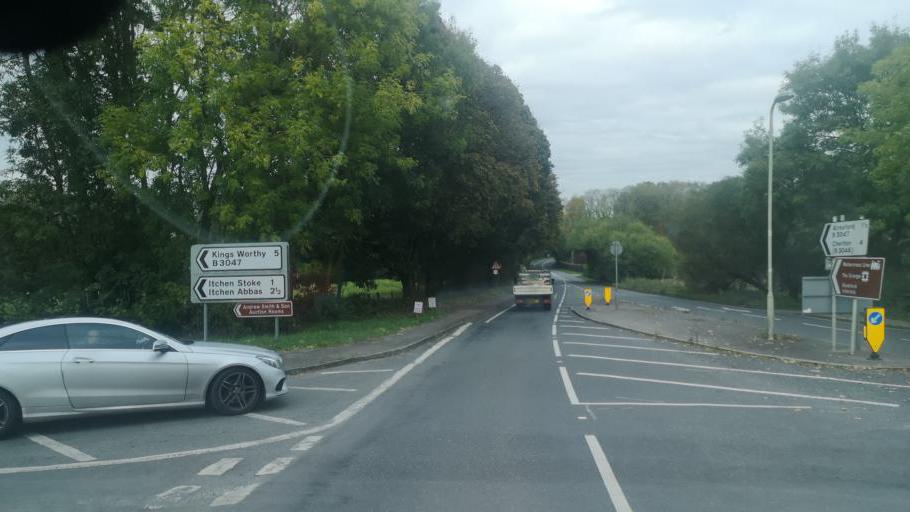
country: GB
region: England
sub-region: Hampshire
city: Kings Worthy
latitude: 51.0849
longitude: -1.1841
